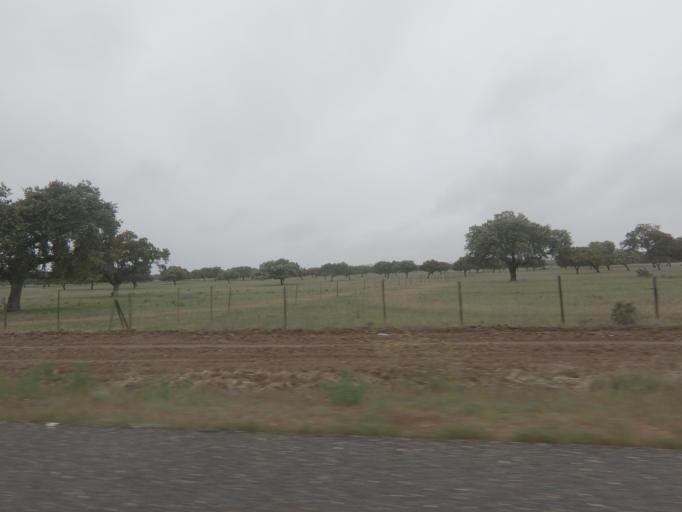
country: ES
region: Extremadura
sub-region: Provincia de Badajoz
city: La Roca de la Sierra
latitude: 39.0859
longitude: -6.7318
